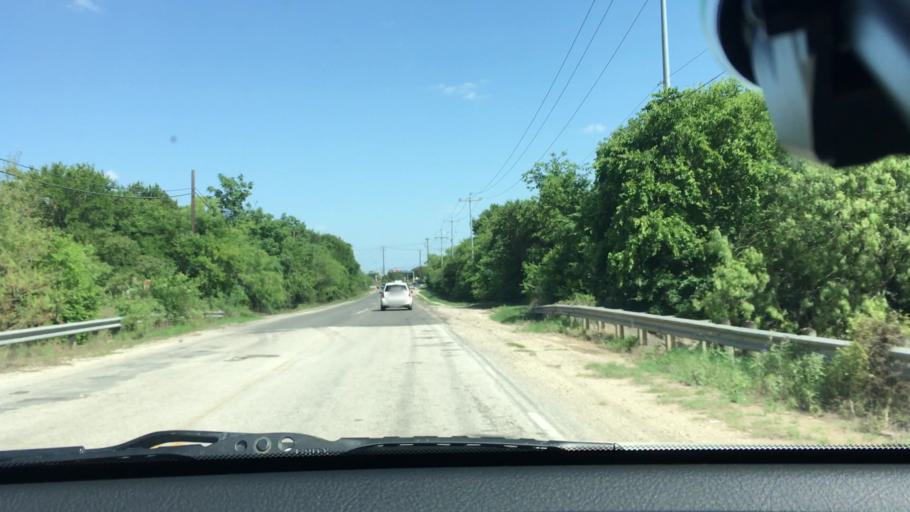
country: US
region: Texas
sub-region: Bexar County
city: Selma
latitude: 29.6067
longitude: -98.3303
